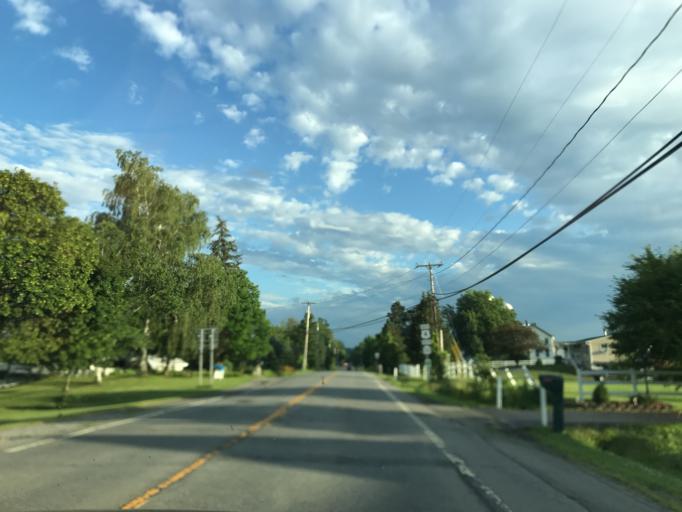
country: US
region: New York
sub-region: Saratoga County
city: Stillwater
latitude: 42.9705
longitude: -73.6334
